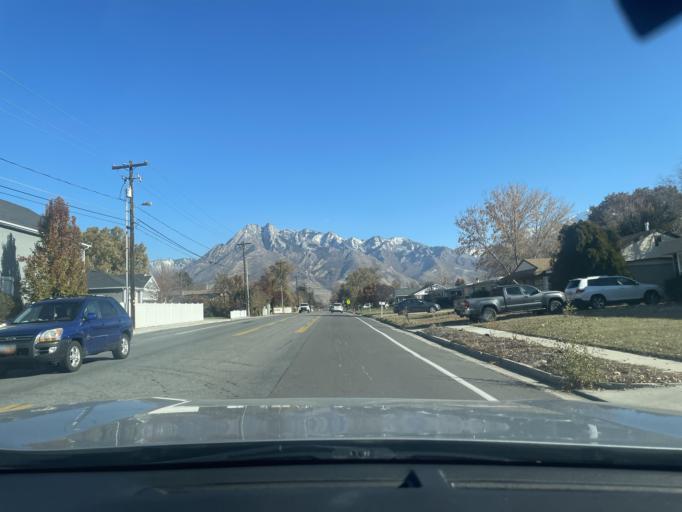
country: US
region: Utah
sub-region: Salt Lake County
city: Murray
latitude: 40.6495
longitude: -111.8636
